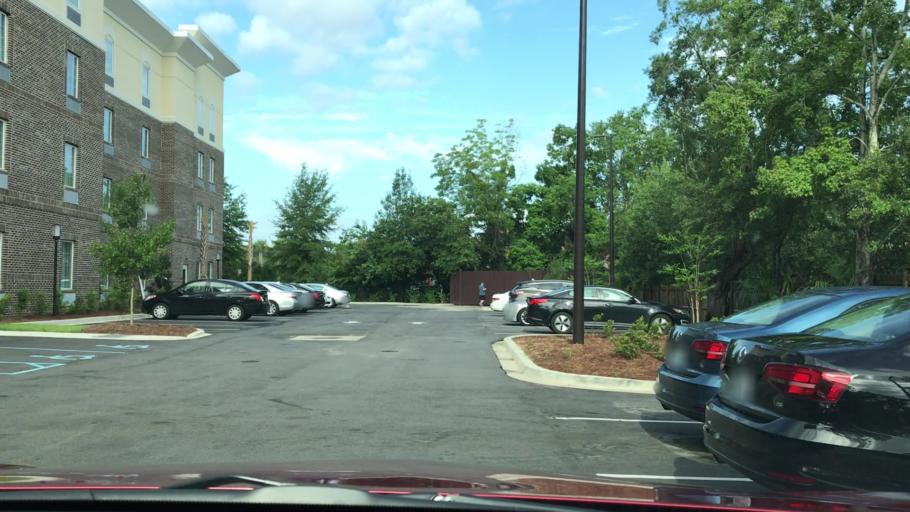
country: US
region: South Carolina
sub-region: Charleston County
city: Shell Point
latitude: 32.7930
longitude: -80.0282
